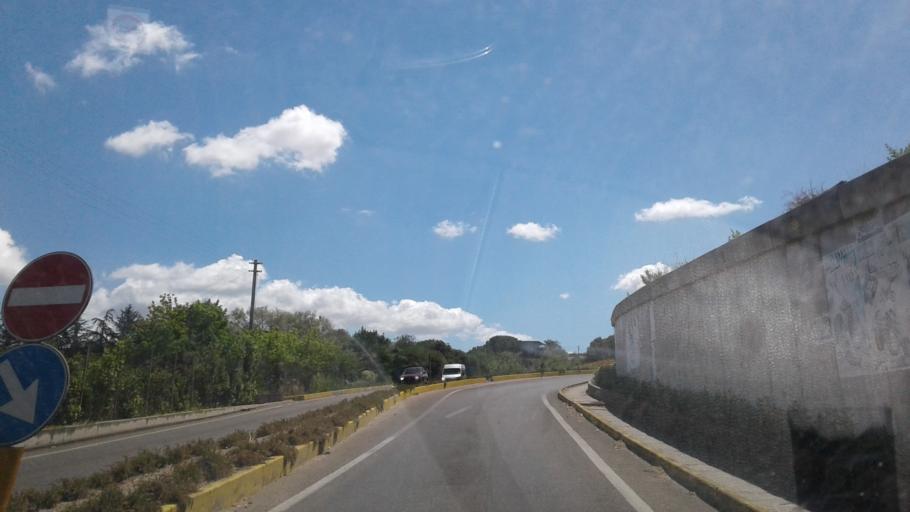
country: IT
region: Sardinia
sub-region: Provincia di Olbia-Tempio
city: Tempio Pausania
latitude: 40.9047
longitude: 9.1210
